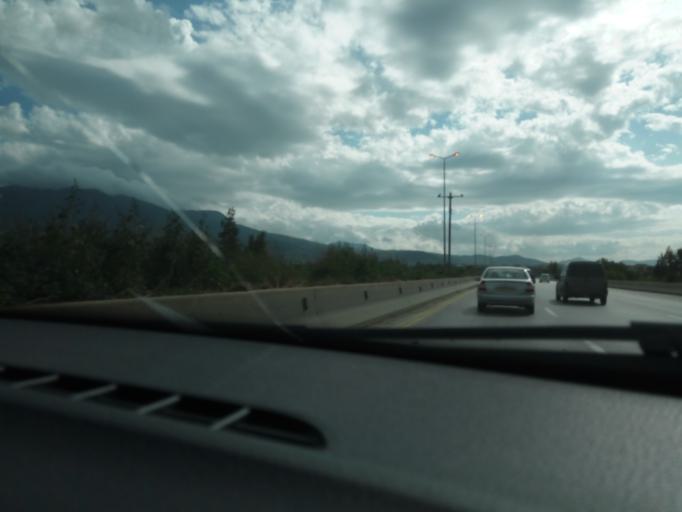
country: DZ
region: Blida
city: Chiffa
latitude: 36.4600
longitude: 2.7514
